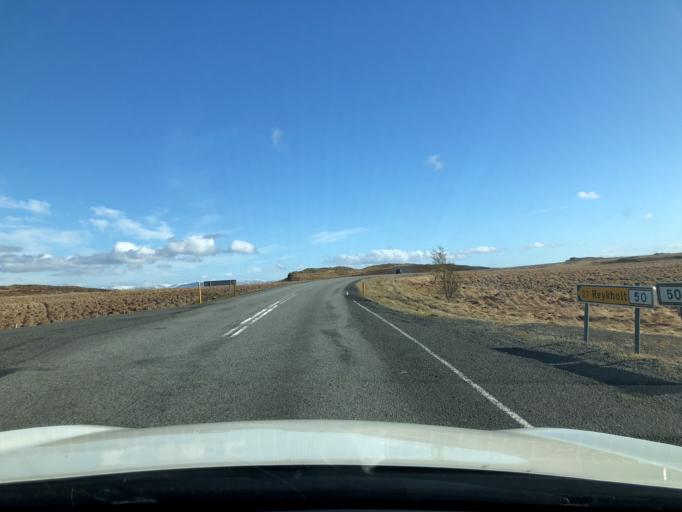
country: IS
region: West
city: Borgarnes
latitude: 64.5560
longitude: -21.7316
